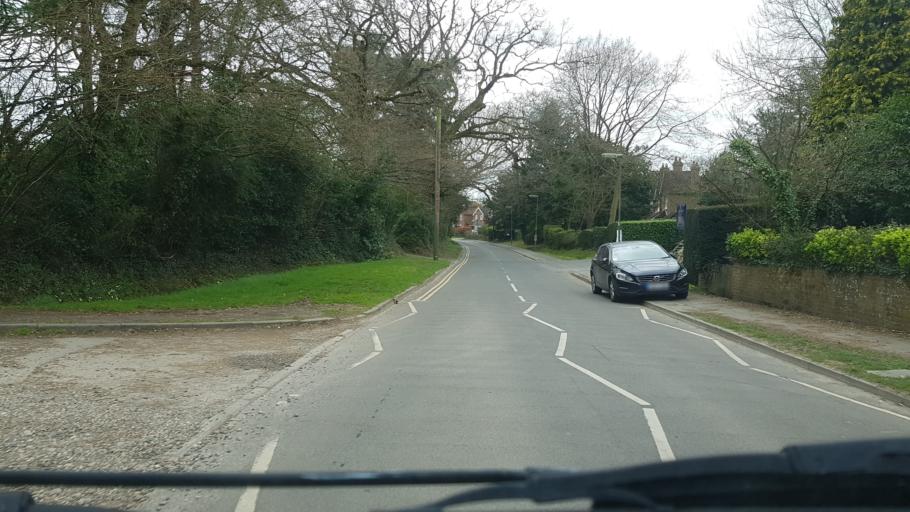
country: GB
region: England
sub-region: Surrey
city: Cranleigh
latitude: 51.1480
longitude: -0.4944
